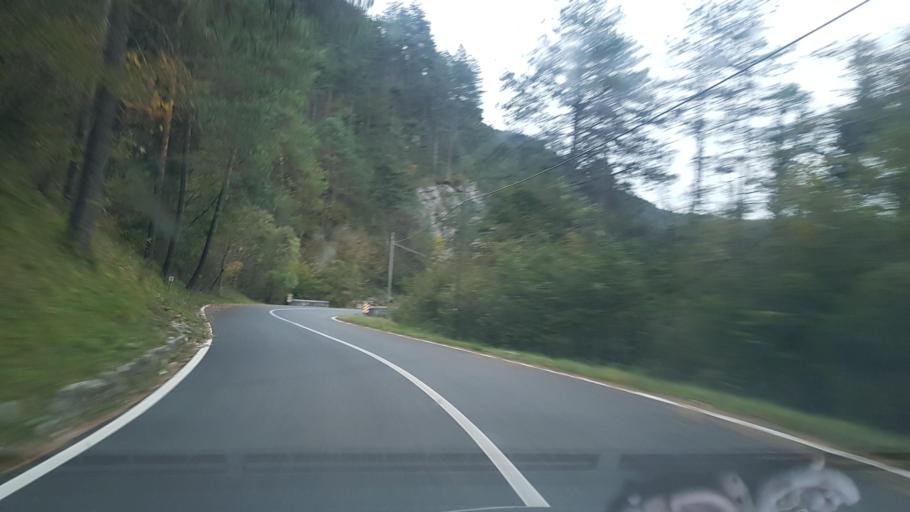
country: IT
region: Friuli Venezia Giulia
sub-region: Provincia di Pordenone
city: Anduins
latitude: 46.2877
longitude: 12.9342
